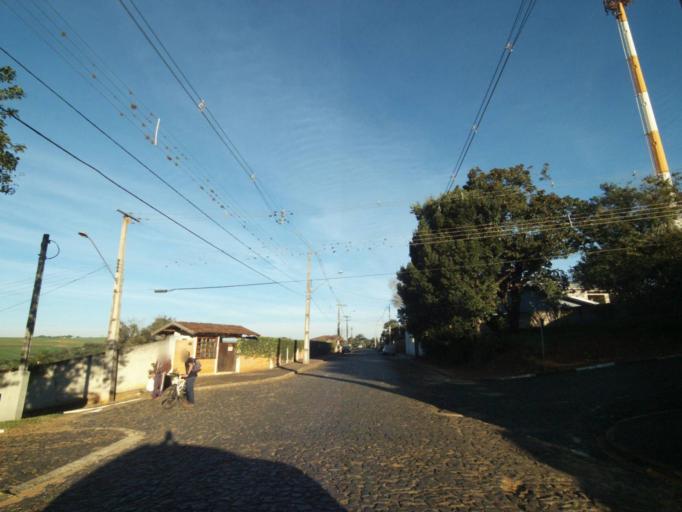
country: BR
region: Parana
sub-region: Tibagi
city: Tibagi
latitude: -24.5152
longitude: -50.4082
